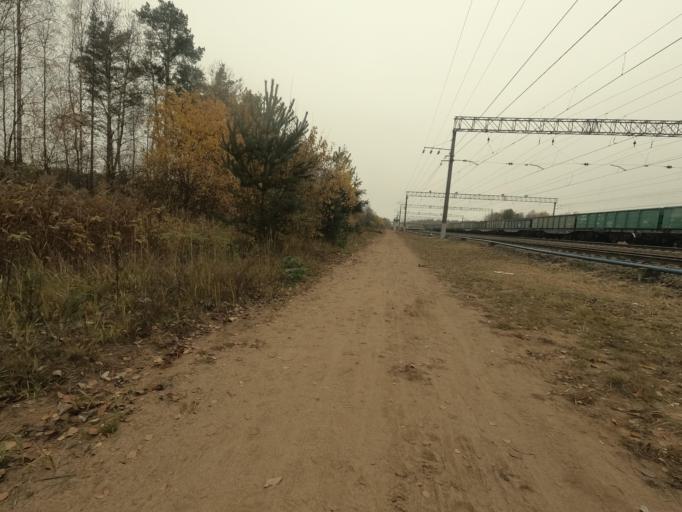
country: RU
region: Leningrad
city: Pavlovo
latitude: 59.7668
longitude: 30.9524
